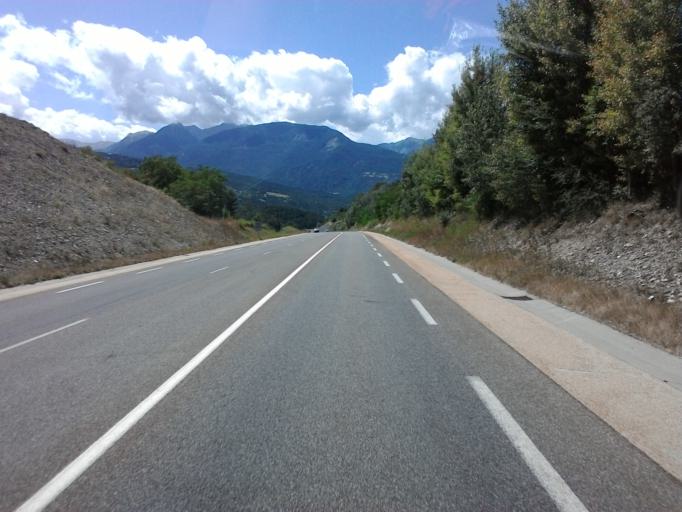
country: FR
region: Provence-Alpes-Cote d'Azur
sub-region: Departement des Hautes-Alpes
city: Embrun
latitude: 44.5787
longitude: 6.5112
